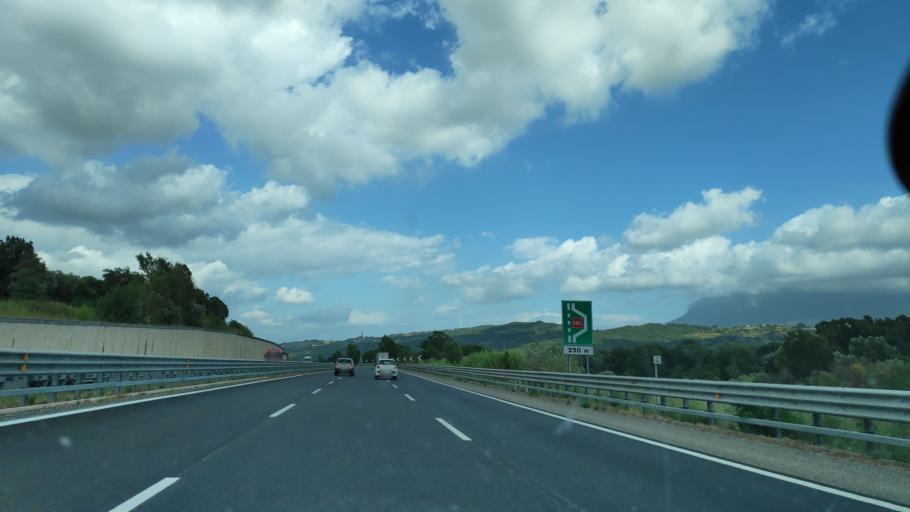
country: IT
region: Campania
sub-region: Provincia di Salerno
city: Quadrivio
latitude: 40.6134
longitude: 15.1456
